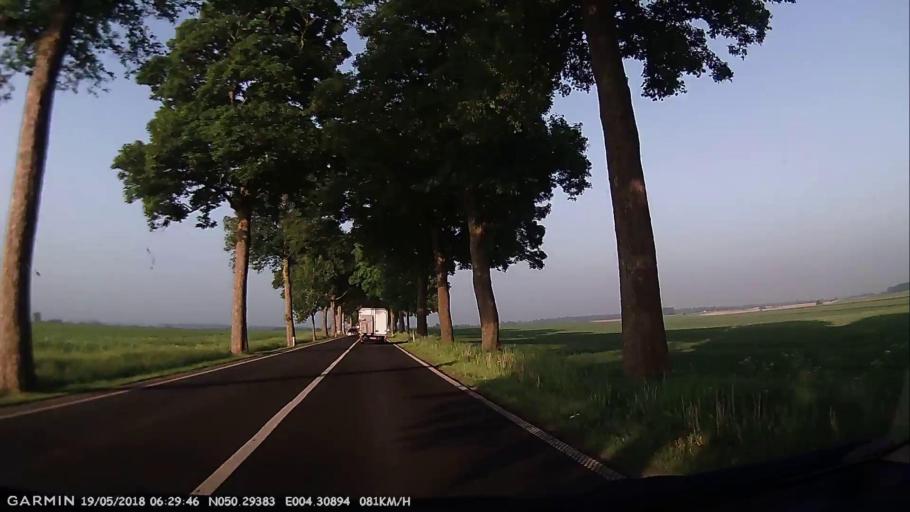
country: BE
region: Wallonia
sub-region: Province du Hainaut
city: Thuin
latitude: 50.2937
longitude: 4.3088
